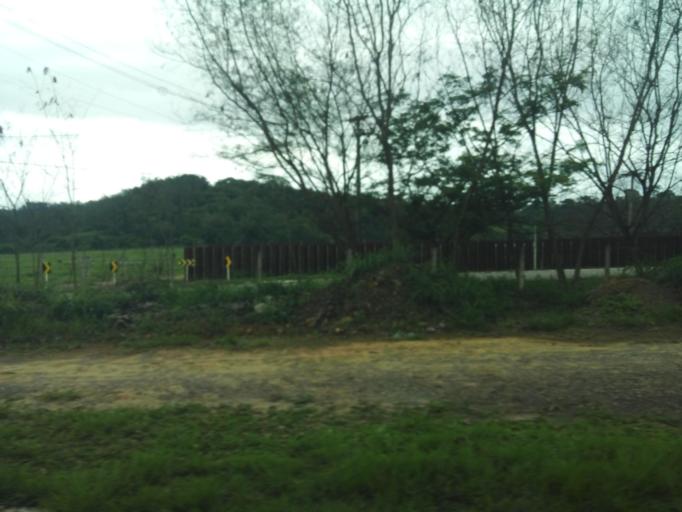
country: BR
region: Minas Gerais
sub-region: Ipatinga
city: Ipatinga
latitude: -19.4805
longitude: -42.4912
